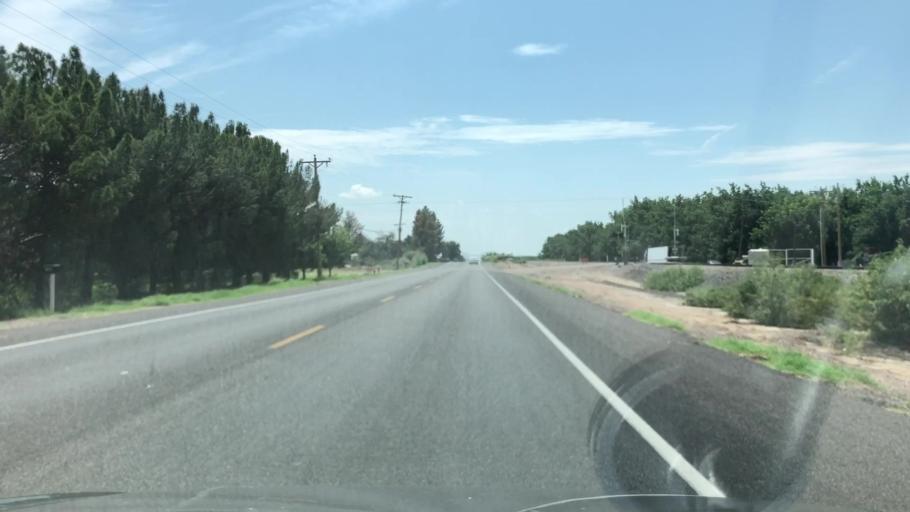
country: US
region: New Mexico
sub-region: Dona Ana County
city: Mesquite
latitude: 32.2045
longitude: -106.7218
